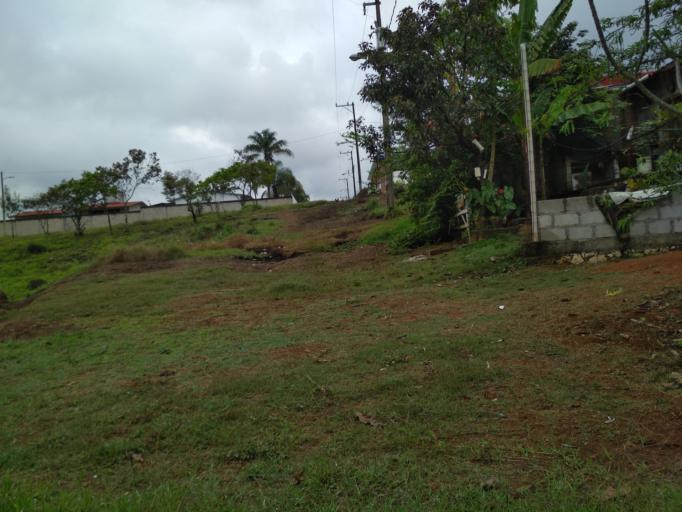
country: MX
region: Veracruz
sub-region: Cordoba
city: San Jose de Tapia
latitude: 18.8486
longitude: -96.9662
